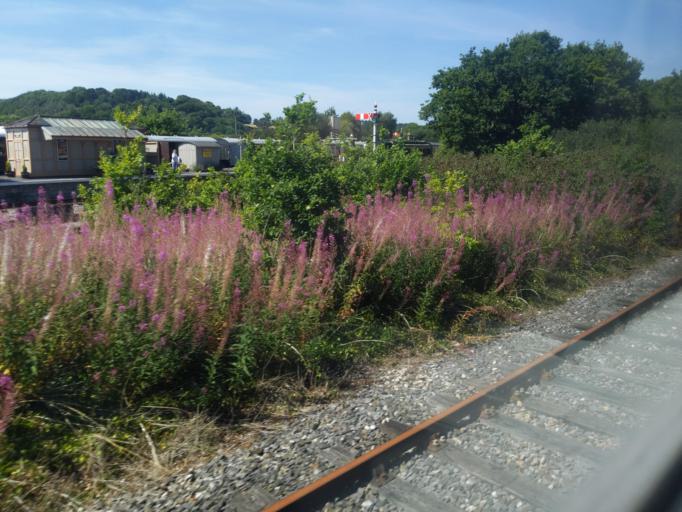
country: GB
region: England
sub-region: Devon
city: Totnes
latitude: 50.4394
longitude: -3.6853
